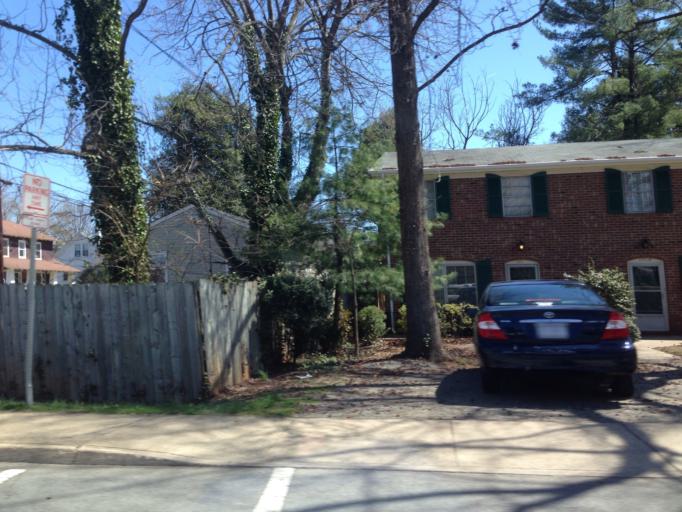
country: US
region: Virginia
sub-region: City of Charlottesville
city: Charlottesville
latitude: 38.0241
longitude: -78.5148
